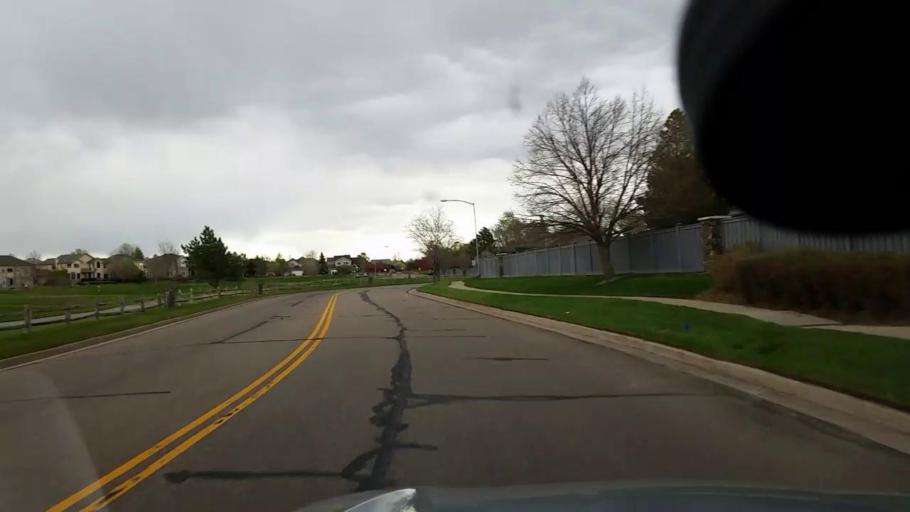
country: US
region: Colorado
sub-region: Adams County
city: Northglenn
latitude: 39.9397
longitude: -104.9749
